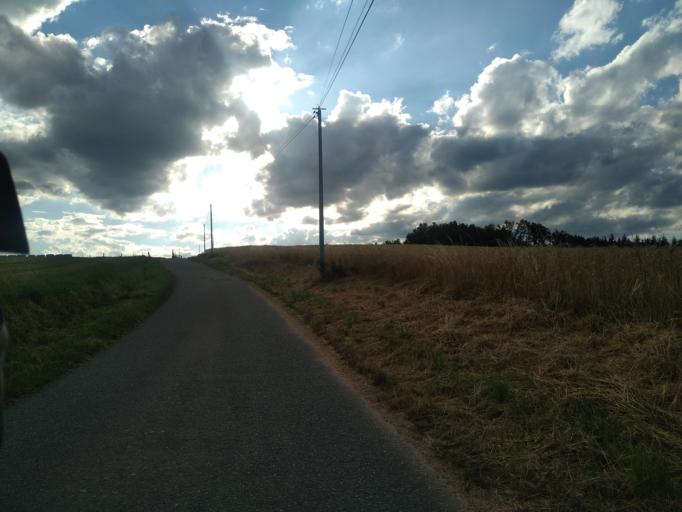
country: FR
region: Rhone-Alpes
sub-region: Departement de la Loire
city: Panissieres
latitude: 45.7433
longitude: 4.3343
